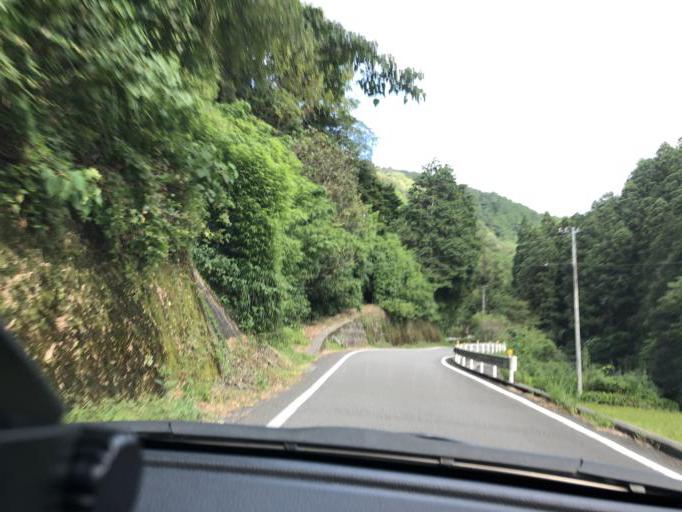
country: JP
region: Kochi
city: Kochi-shi
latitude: 33.6110
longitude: 133.5097
